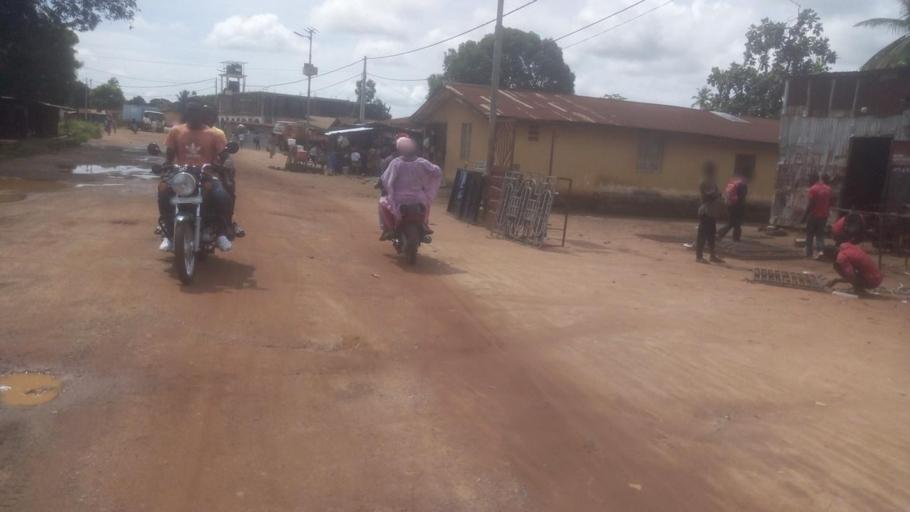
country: SL
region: Northern Province
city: Masoyila
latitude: 8.6017
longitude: -13.1838
